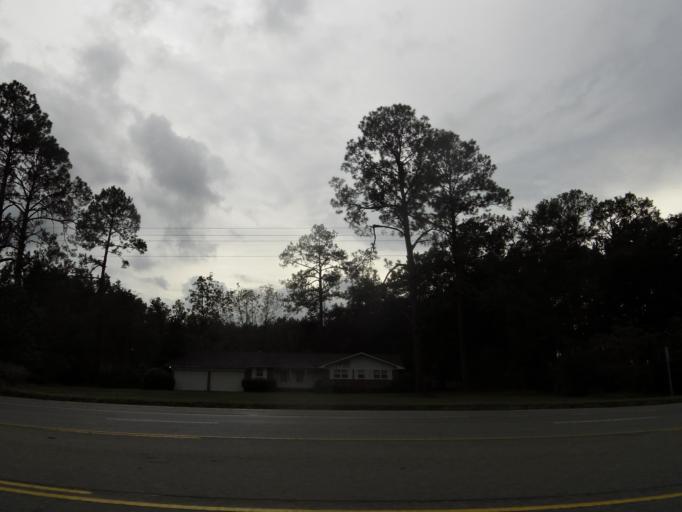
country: US
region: Georgia
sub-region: Wayne County
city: Jesup
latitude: 31.5591
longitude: -81.8292
